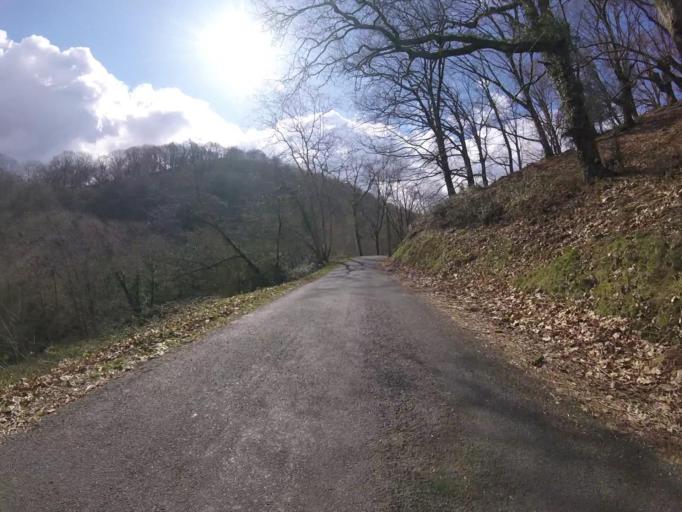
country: FR
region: Aquitaine
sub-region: Departement des Pyrenees-Atlantiques
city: Sare
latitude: 43.2708
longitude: -1.6042
